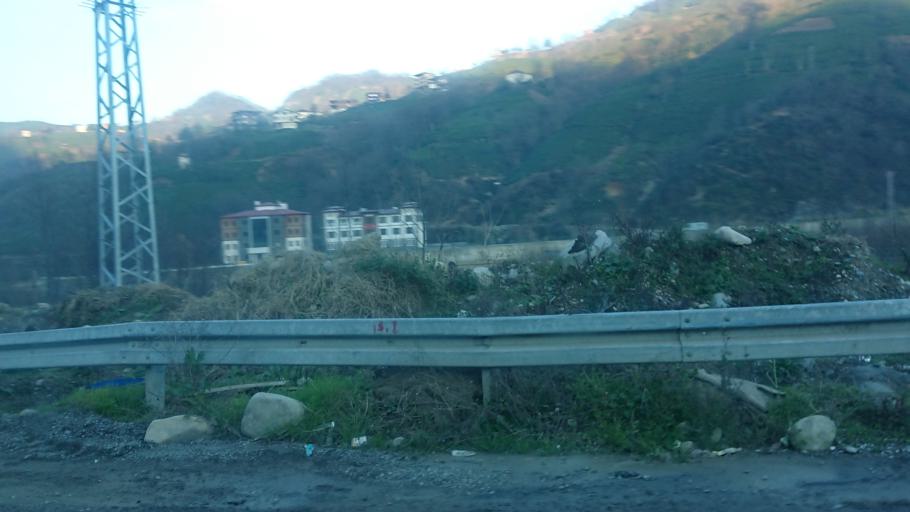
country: TR
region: Rize
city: Gundogdu
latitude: 41.0201
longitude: 40.5745
